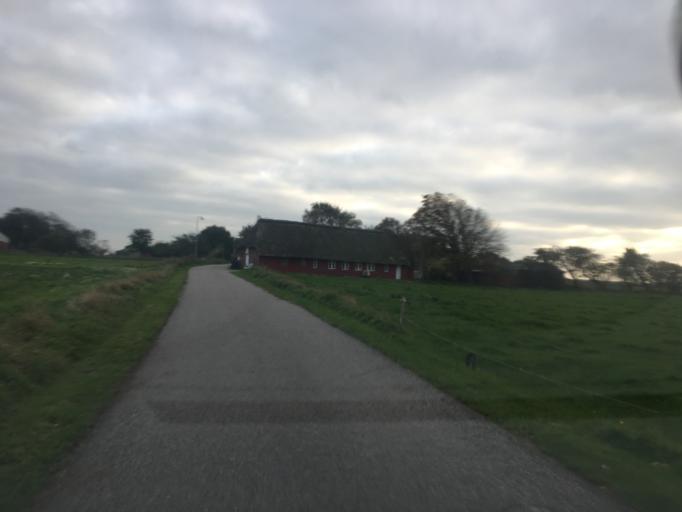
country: DE
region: Schleswig-Holstein
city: Rodenas
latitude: 54.9685
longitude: 8.7383
